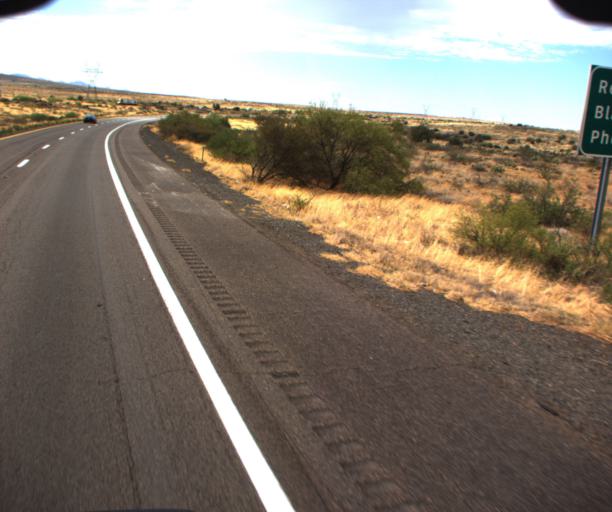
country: US
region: Arizona
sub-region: Yavapai County
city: Cordes Lakes
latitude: 34.2224
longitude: -112.1125
